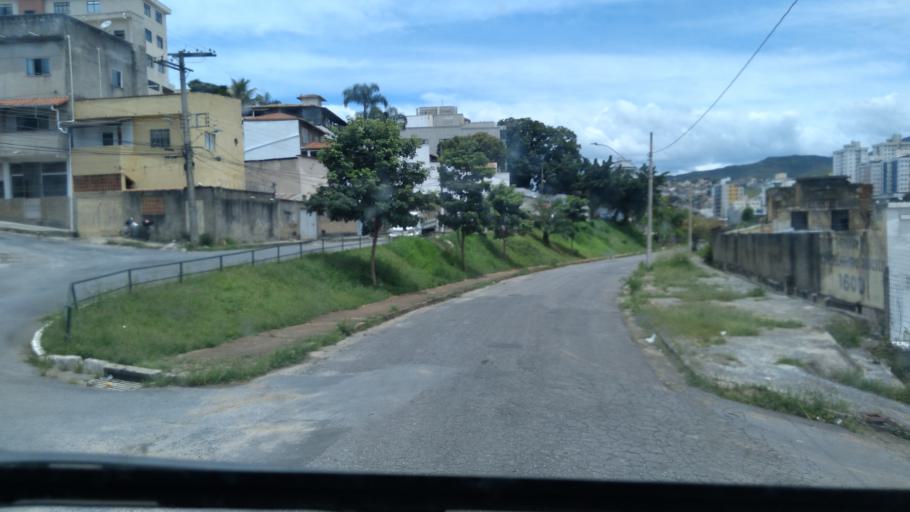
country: BR
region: Minas Gerais
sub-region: Belo Horizonte
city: Belo Horizonte
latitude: -19.9176
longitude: -43.9191
